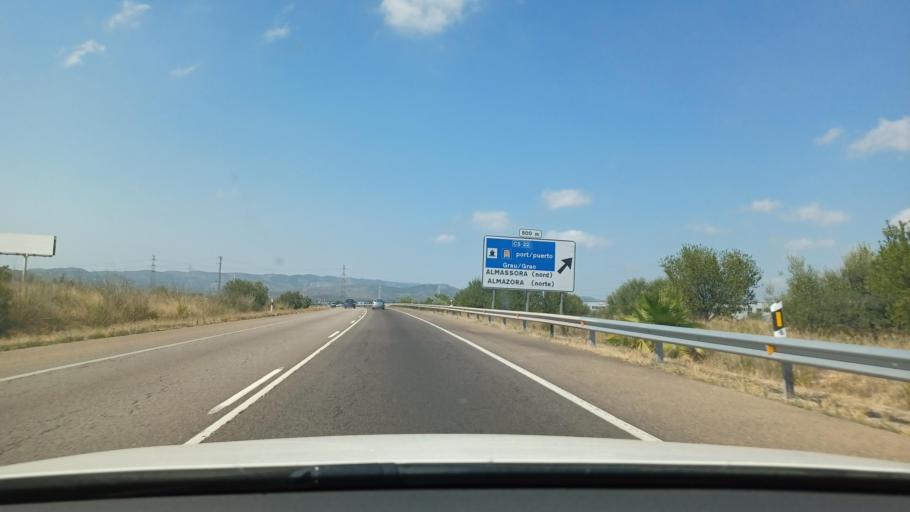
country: ES
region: Valencia
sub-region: Provincia de Castello
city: Vila-real
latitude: 39.9631
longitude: -0.0854
